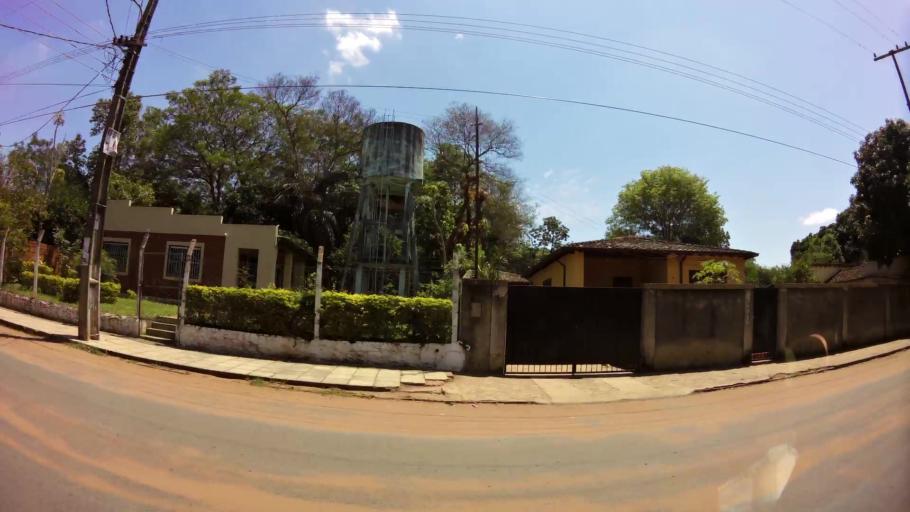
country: PY
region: Central
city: San Antonio
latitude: -25.4253
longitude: -57.5324
